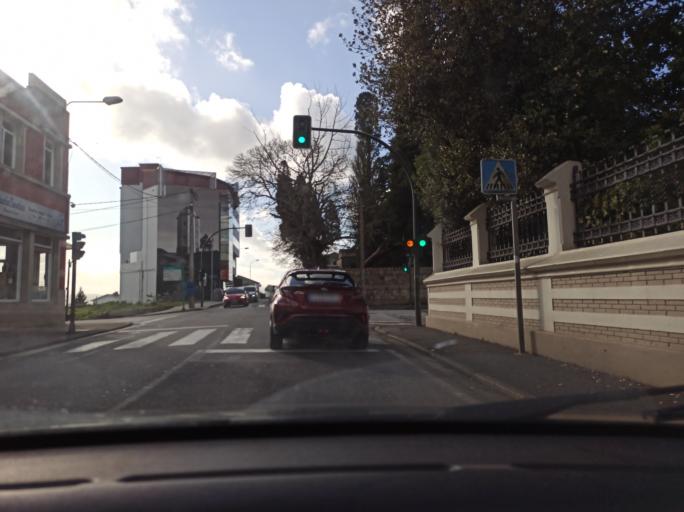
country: ES
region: Galicia
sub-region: Provincia da Coruna
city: Oleiros
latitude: 43.3328
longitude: -8.3152
